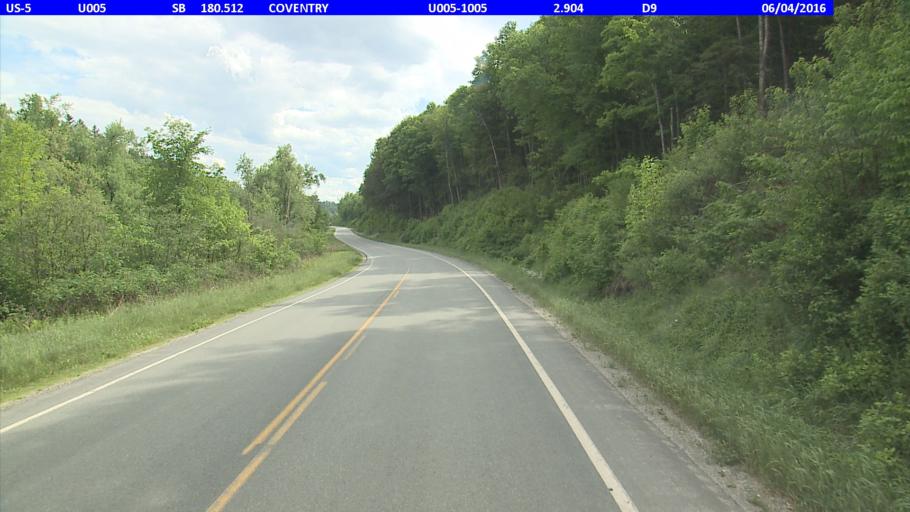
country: US
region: Vermont
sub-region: Orleans County
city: Newport
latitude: 44.8974
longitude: -72.2449
